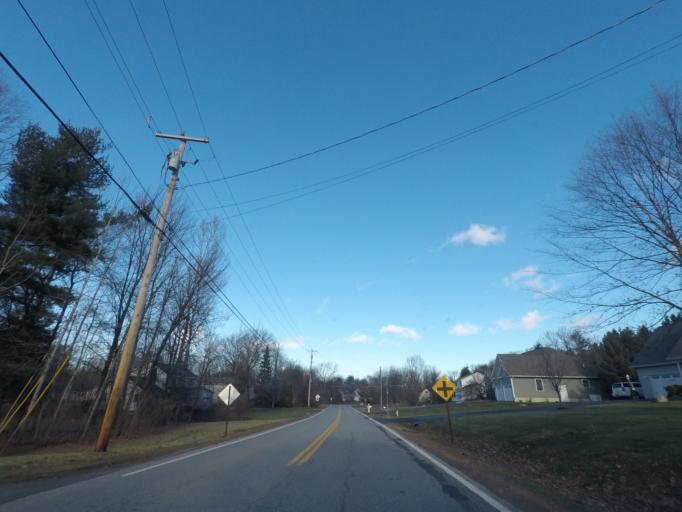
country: US
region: New York
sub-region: Saratoga County
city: Country Knolls
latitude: 42.8788
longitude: -73.7514
